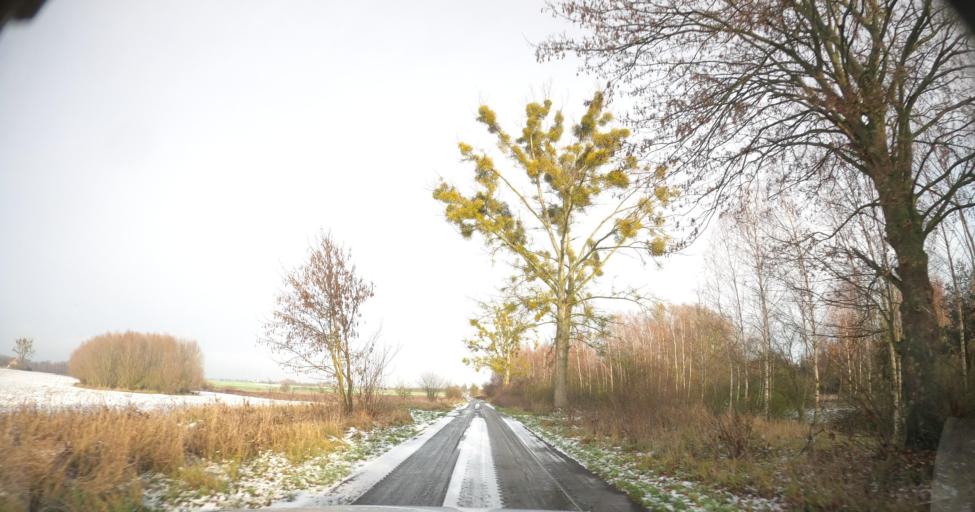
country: PL
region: West Pomeranian Voivodeship
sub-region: Powiat gryfinski
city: Mieszkowice
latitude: 52.7695
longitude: 14.4880
